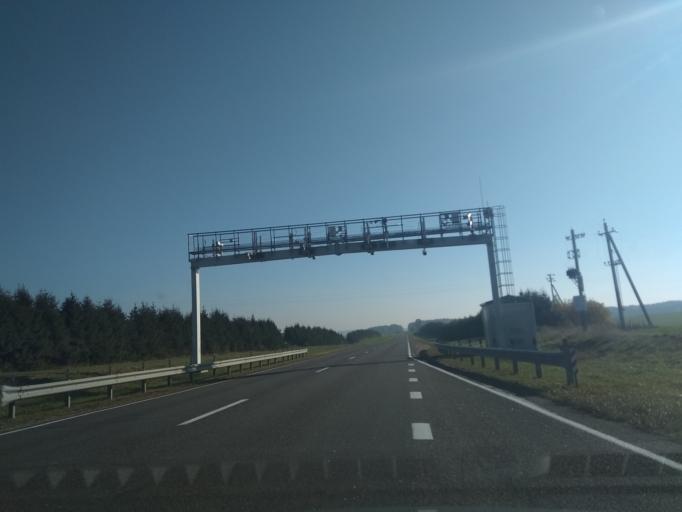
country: BY
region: Grodnenskaya
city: Zel'va
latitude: 53.1348
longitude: 24.9760
